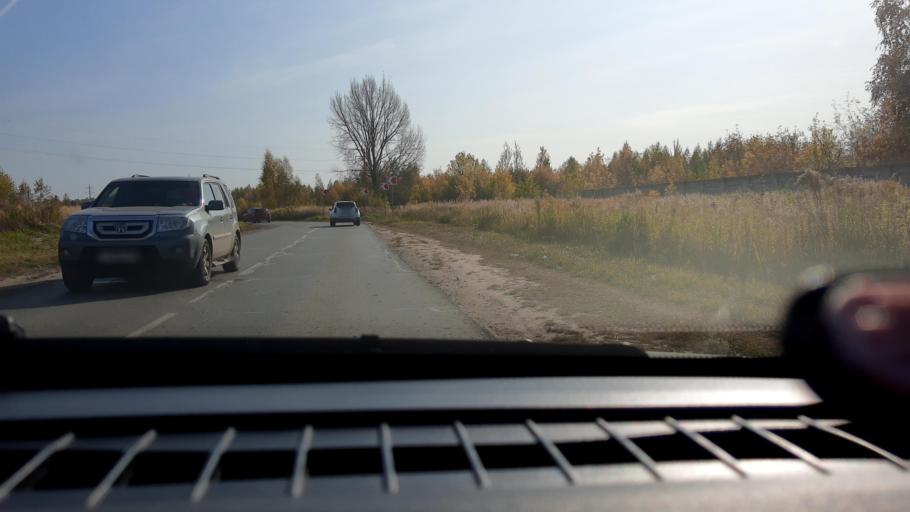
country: RU
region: Nizjnij Novgorod
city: Kstovo
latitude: 56.1482
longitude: 44.2268
